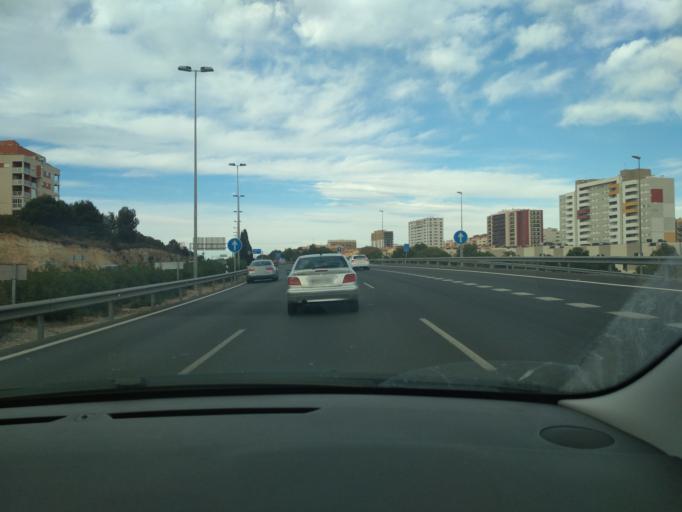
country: ES
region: Valencia
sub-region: Provincia de Valencia
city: Burjassot
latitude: 39.5162
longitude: -0.4319
